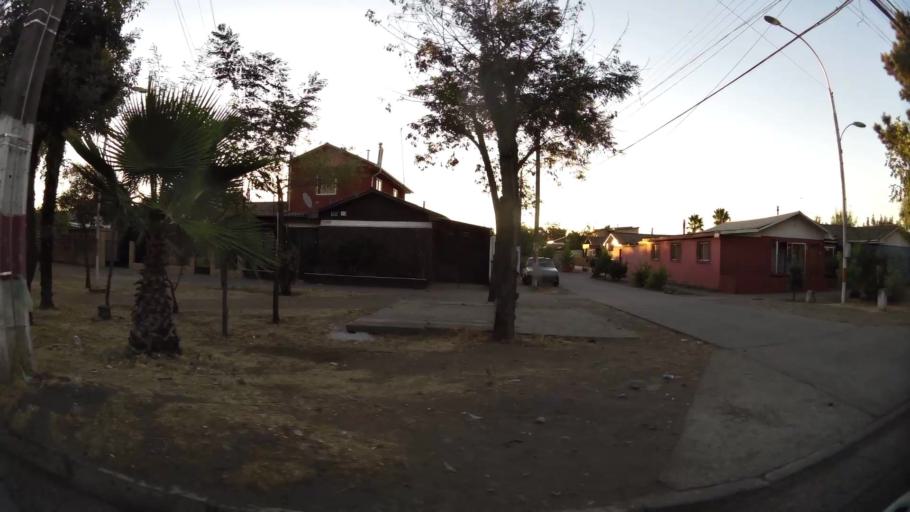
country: CL
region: Maule
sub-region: Provincia de Curico
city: Curico
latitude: -34.9786
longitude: -71.2351
